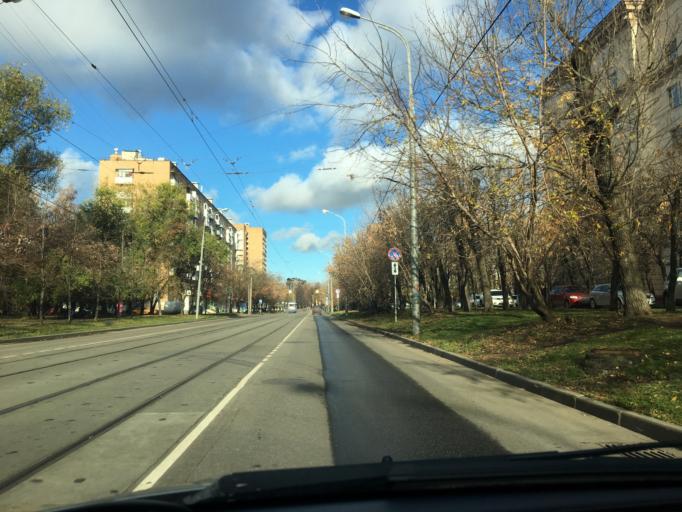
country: RU
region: Moscow
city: Likhobory
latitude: 55.8142
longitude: 37.5708
